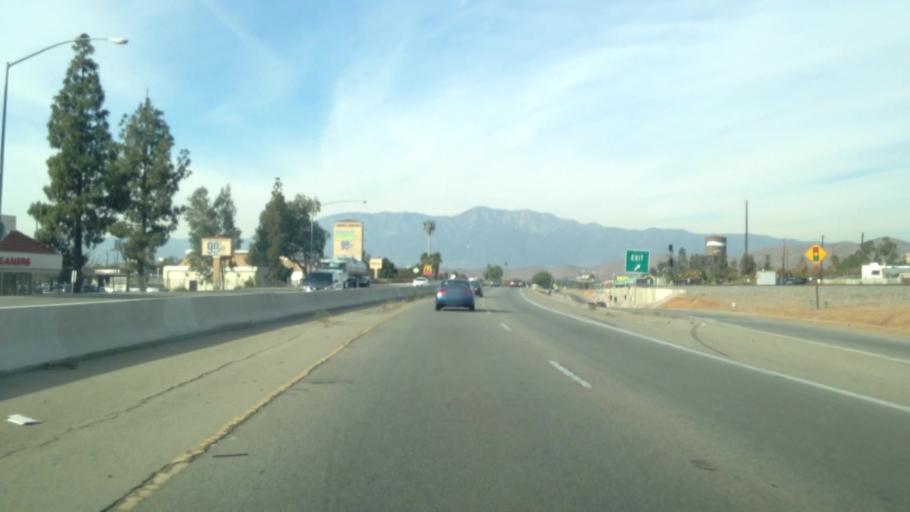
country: US
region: California
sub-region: Riverside County
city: Pedley
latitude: 33.9737
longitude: -117.4752
